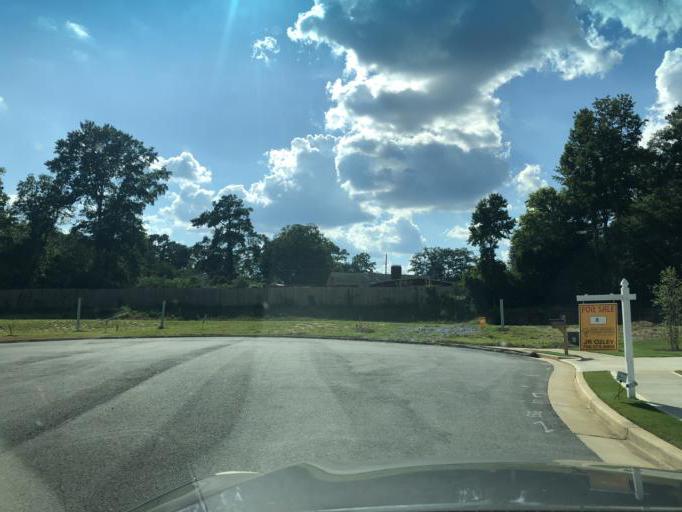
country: US
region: Georgia
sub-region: Muscogee County
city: Columbus
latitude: 32.4999
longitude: -84.9086
